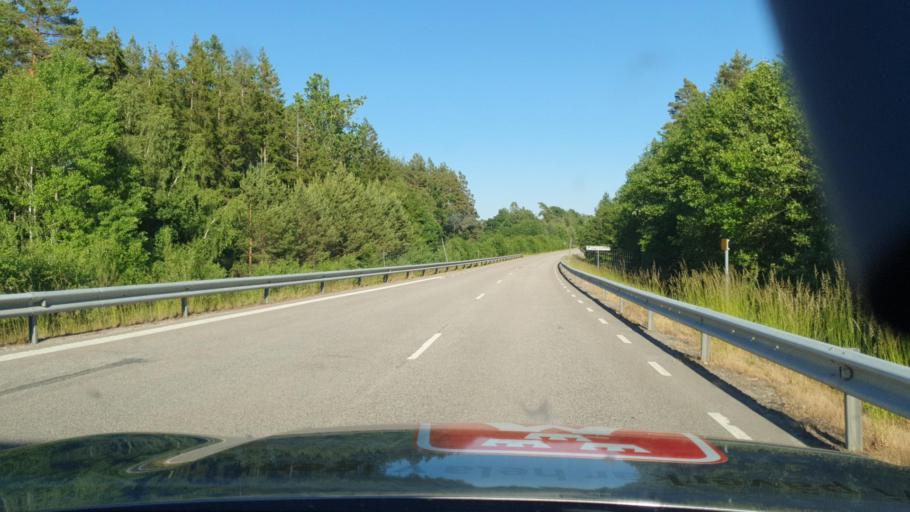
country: SE
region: Kalmar
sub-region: Torsas Kommun
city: Torsas
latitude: 56.5020
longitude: 16.0902
